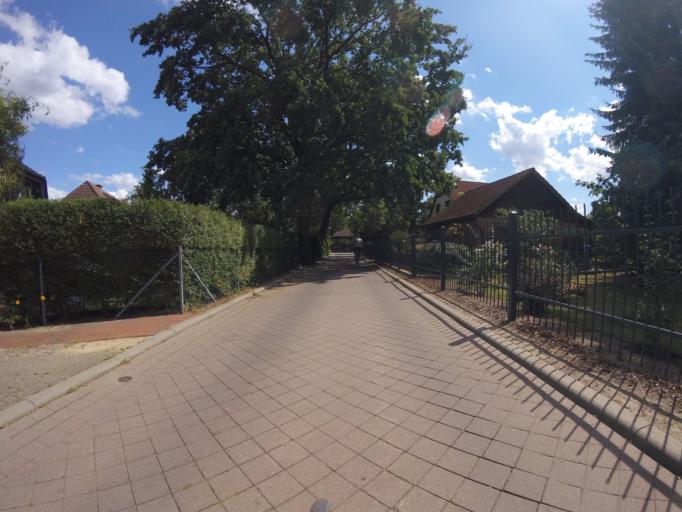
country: DE
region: Brandenburg
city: Werder
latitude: 52.4078
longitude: 12.9903
